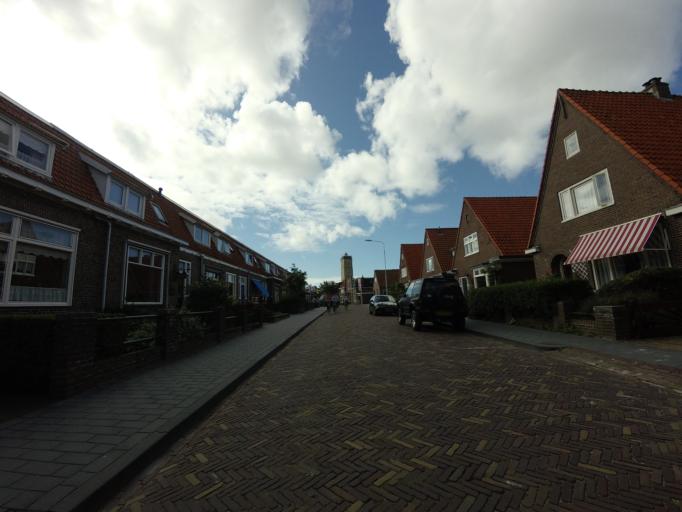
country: NL
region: Friesland
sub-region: Gemeente Terschelling
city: West-Terschelling
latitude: 53.3627
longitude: 5.2165
